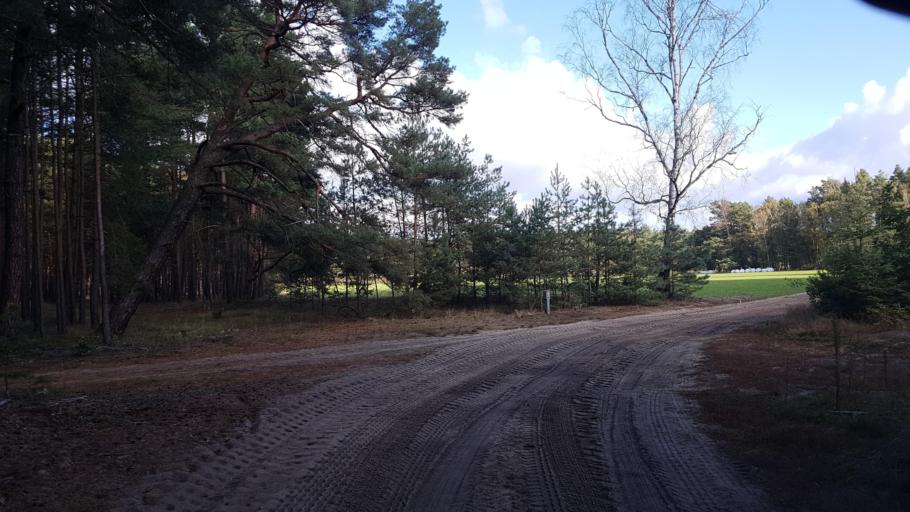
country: DE
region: Brandenburg
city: Vetschau
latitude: 51.7292
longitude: 14.0939
